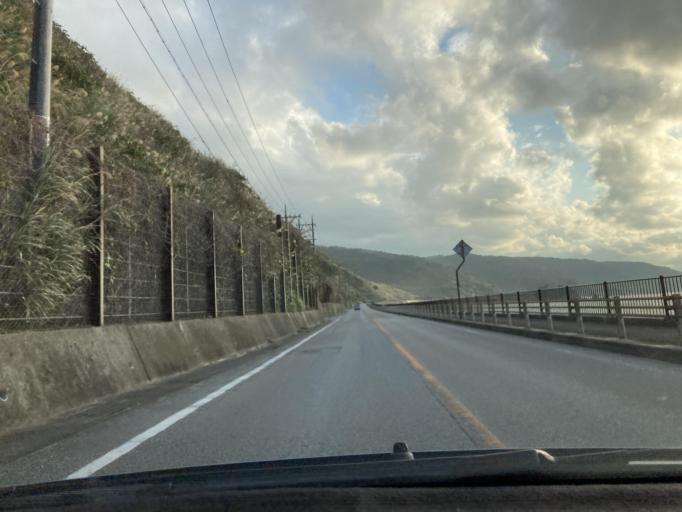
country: JP
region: Okinawa
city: Nago
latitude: 26.7956
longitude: 128.2255
